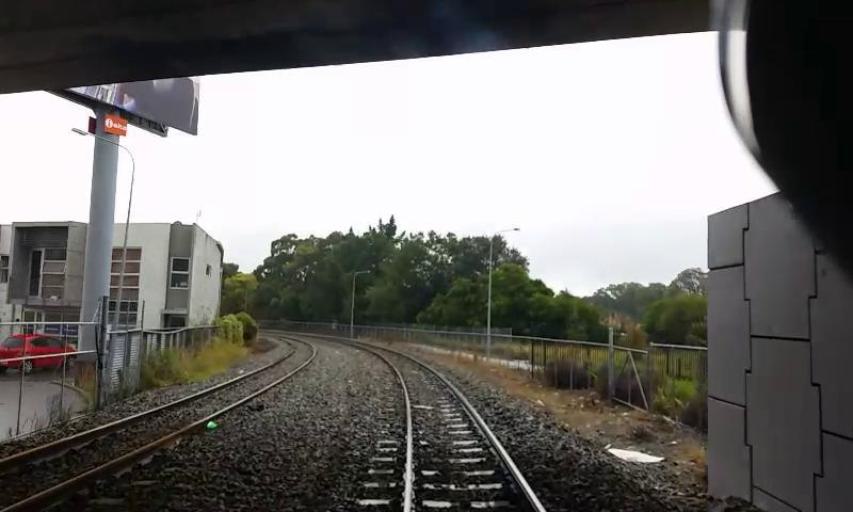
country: NZ
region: Canterbury
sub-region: Christchurch City
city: Christchurch
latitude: -43.5384
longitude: 172.6097
